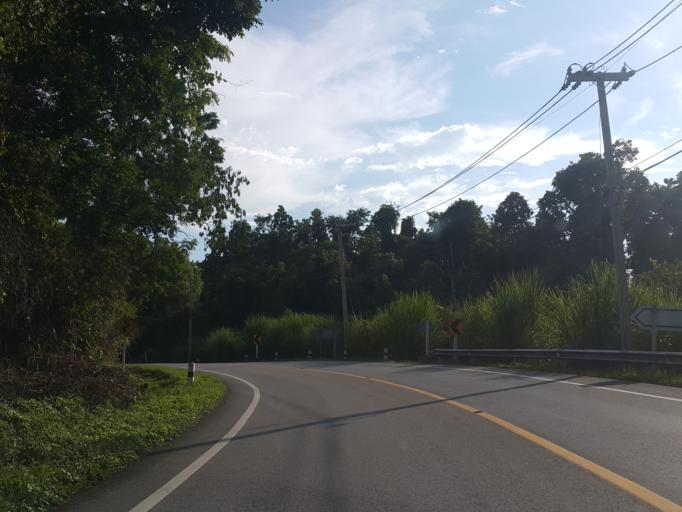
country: TH
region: Chiang Mai
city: Mae Taeng
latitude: 19.0935
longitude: 99.1427
